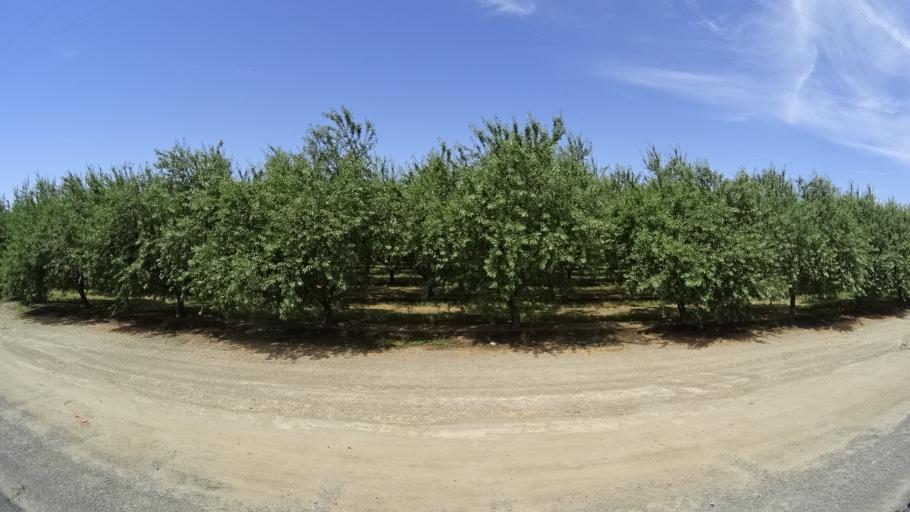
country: US
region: California
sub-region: Kings County
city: Lucerne
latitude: 36.3985
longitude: -119.6910
